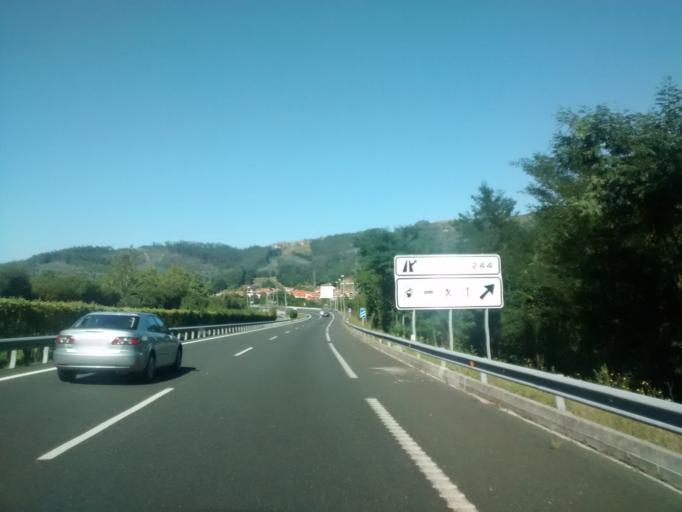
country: ES
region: Cantabria
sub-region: Provincia de Cantabria
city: Luzmela
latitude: 43.3241
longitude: -4.1844
